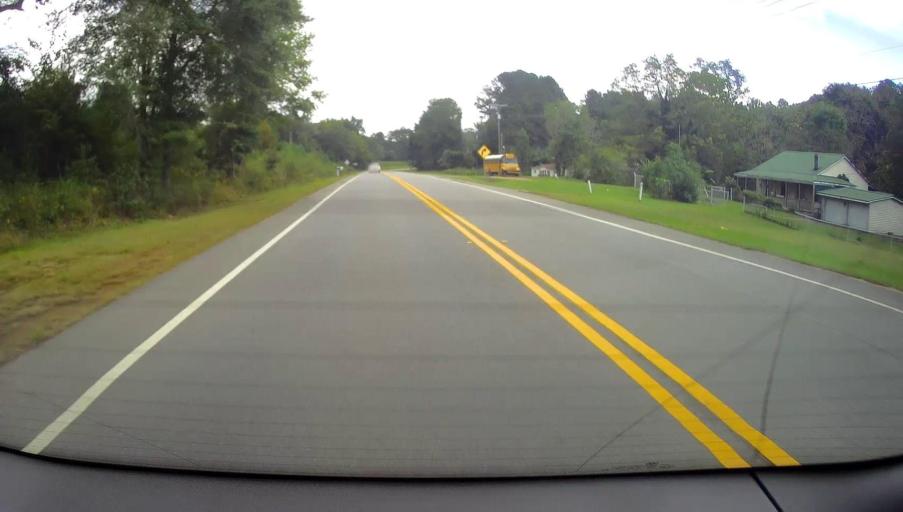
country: US
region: Georgia
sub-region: Baldwin County
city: Milledgeville
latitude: 33.0747
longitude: -83.3364
